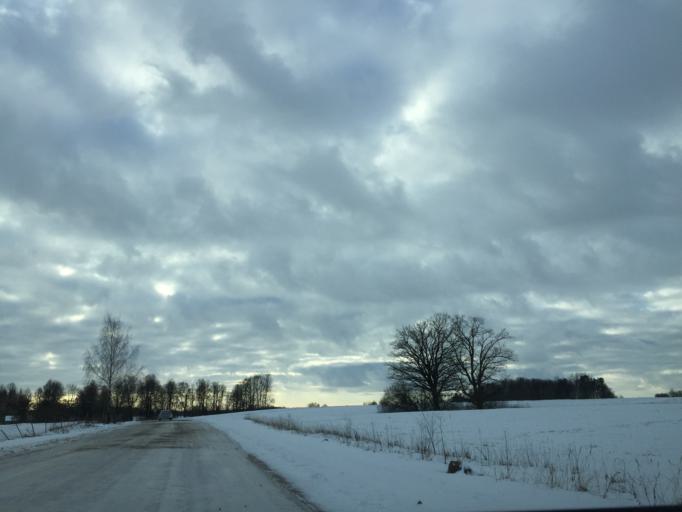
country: LV
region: Lielvarde
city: Lielvarde
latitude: 56.5694
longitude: 24.7336
